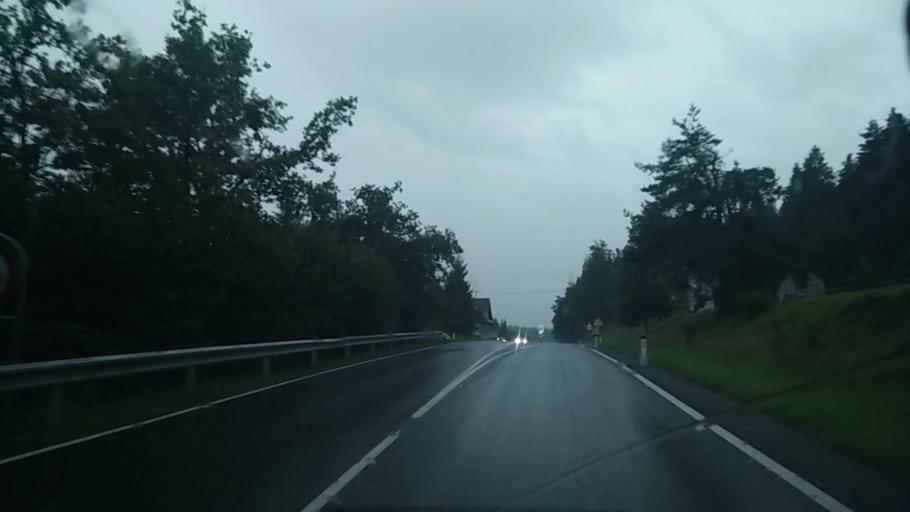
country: AT
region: Carinthia
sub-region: Politischer Bezirk Villach Land
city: Wernberg
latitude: 46.6135
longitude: 13.9716
